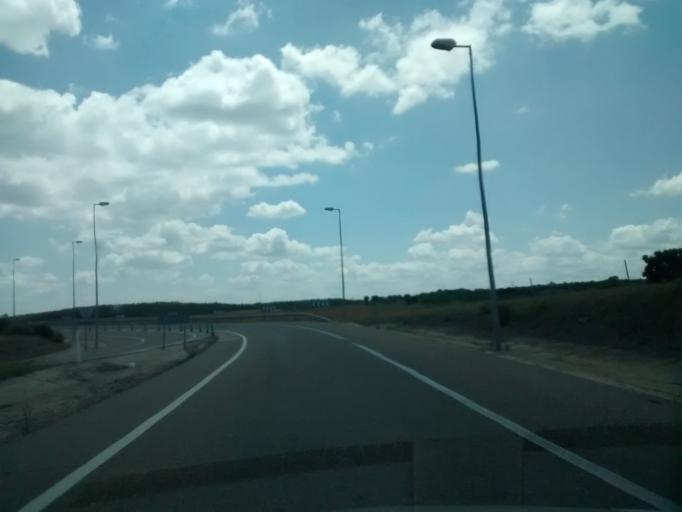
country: ES
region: Castille and Leon
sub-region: Provincia de Leon
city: Astorga
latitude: 42.4363
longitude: -6.0530
